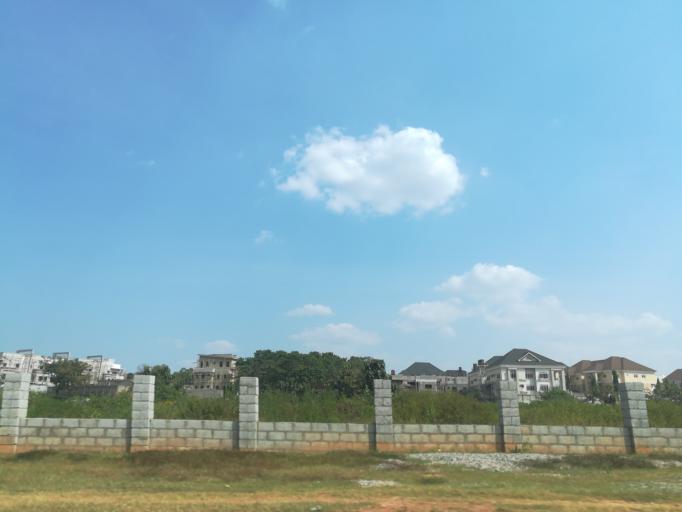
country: NG
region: Abuja Federal Capital Territory
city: Abuja
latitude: 9.0579
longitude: 7.4348
